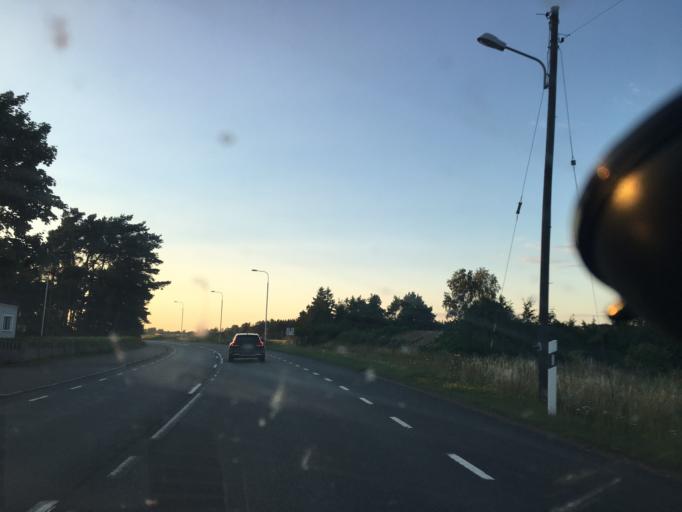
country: SE
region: Skane
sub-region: Kristianstads Kommun
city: Ahus
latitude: 55.9639
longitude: 14.2810
